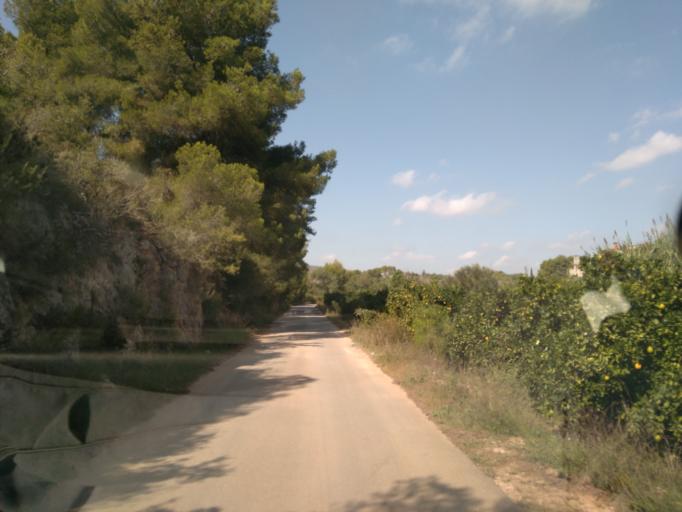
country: ES
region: Valencia
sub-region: Provincia de Valencia
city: Tous
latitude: 39.1768
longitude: -0.5973
